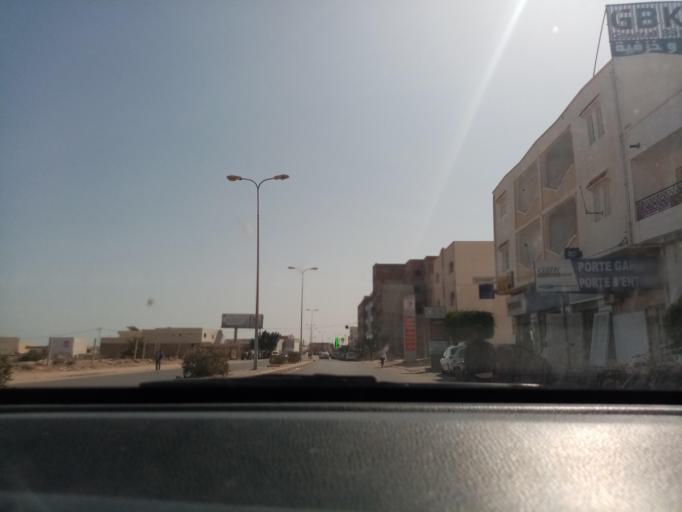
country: TN
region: Qabis
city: Gabes
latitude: 33.8509
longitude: 10.1101
